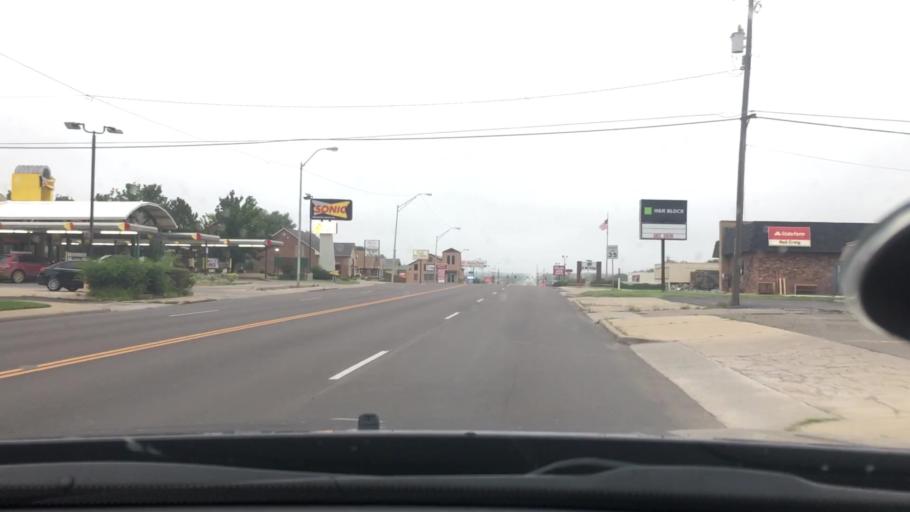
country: US
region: Oklahoma
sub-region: Seminole County
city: Seminole
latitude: 35.2281
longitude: -96.6710
